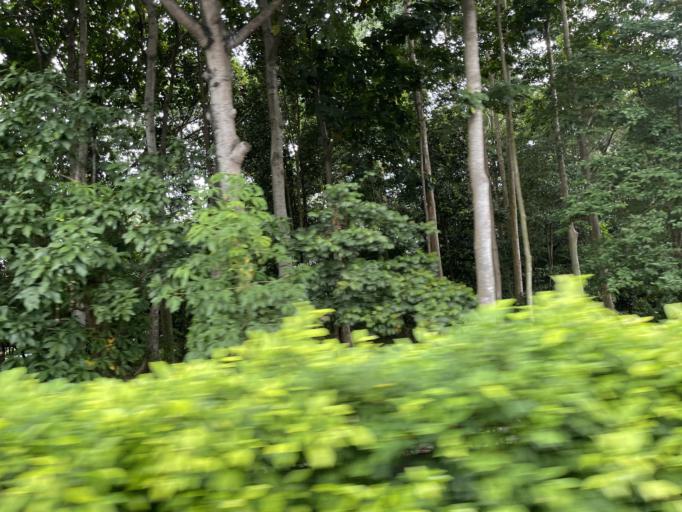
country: SG
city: Singapore
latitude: 1.3051
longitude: 103.7702
